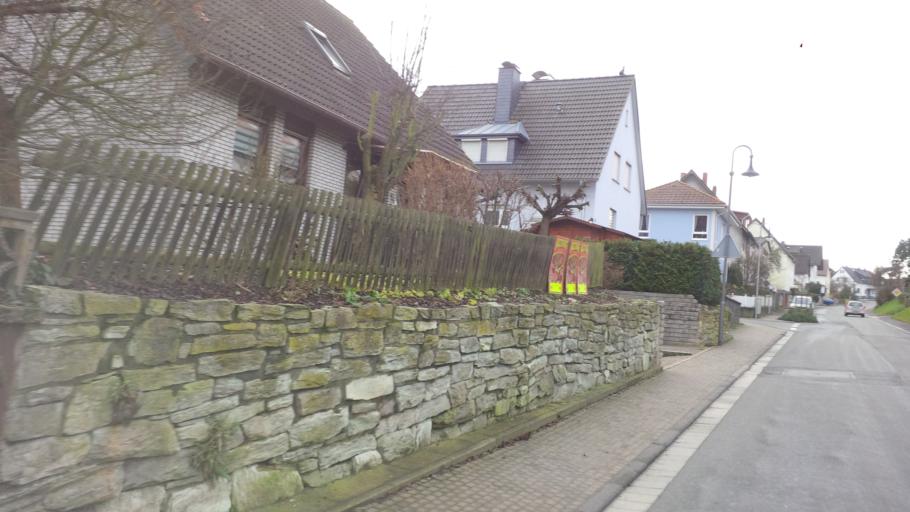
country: DE
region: Hesse
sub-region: Regierungsbezirk Darmstadt
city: Wehrheim
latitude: 50.3291
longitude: 8.6057
